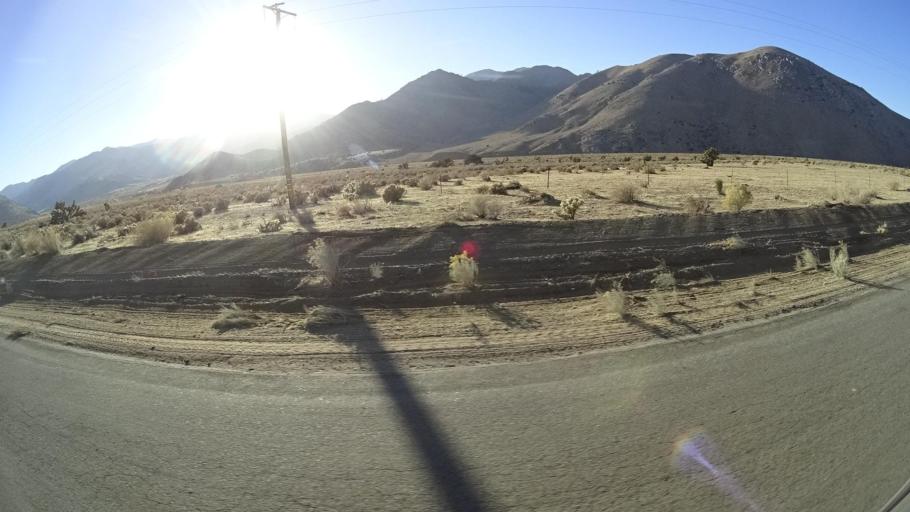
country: US
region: California
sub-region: Kern County
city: Weldon
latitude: 35.6006
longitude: -118.2411
